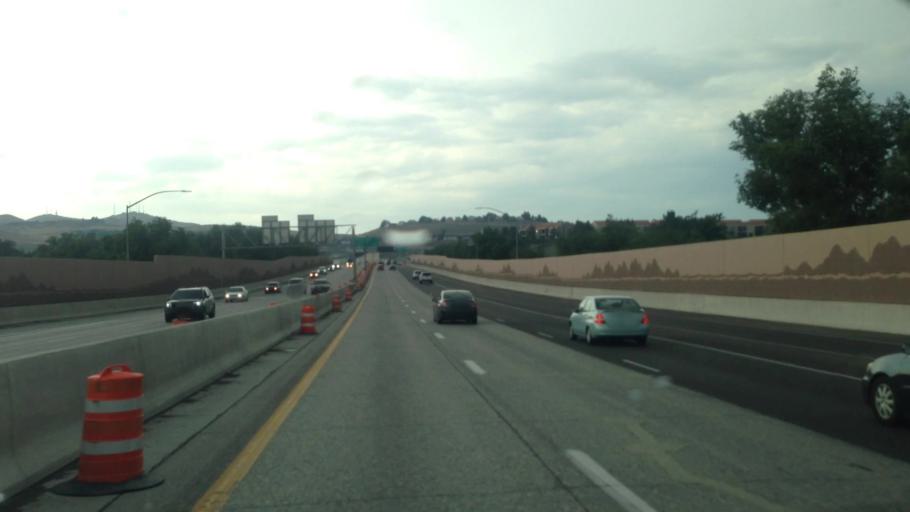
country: US
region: Nevada
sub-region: Washoe County
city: Reno
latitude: 39.5479
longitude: -119.7878
